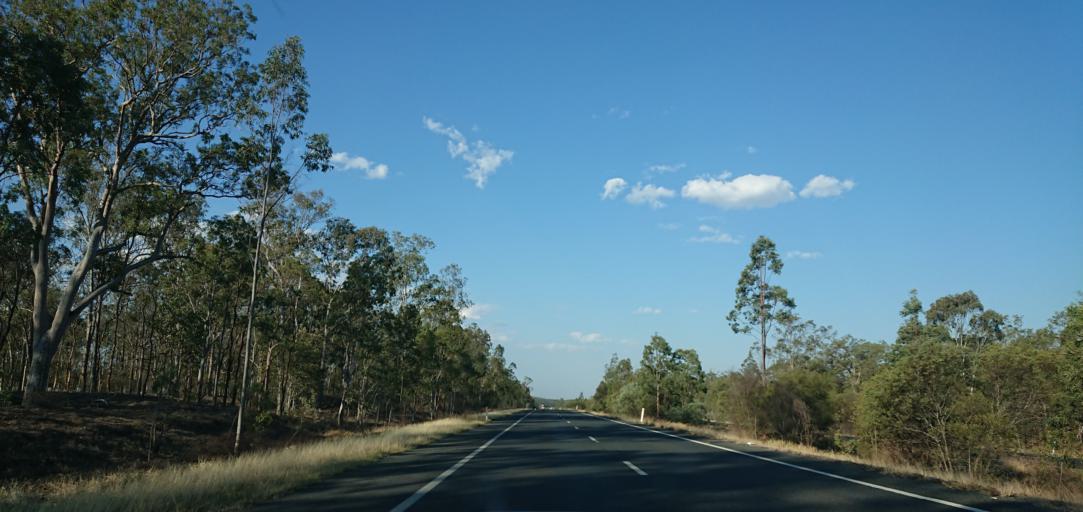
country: AU
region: Queensland
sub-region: Lockyer Valley
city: Gatton
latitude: -27.5453
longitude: 152.2287
